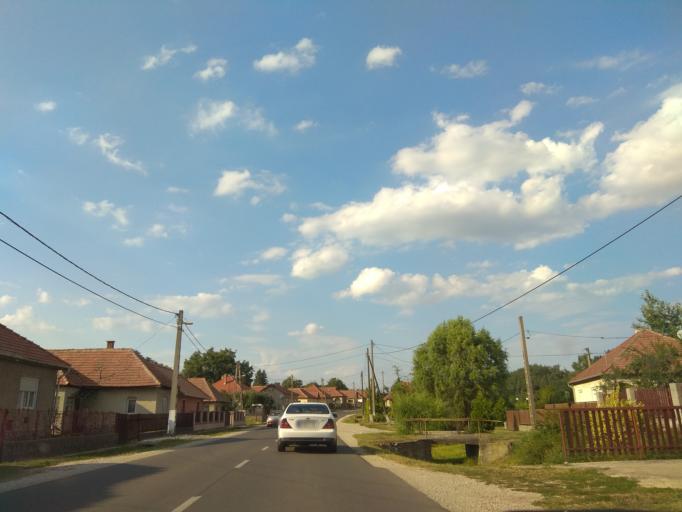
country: HU
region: Borsod-Abauj-Zemplen
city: Harsany
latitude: 47.9732
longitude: 20.7416
